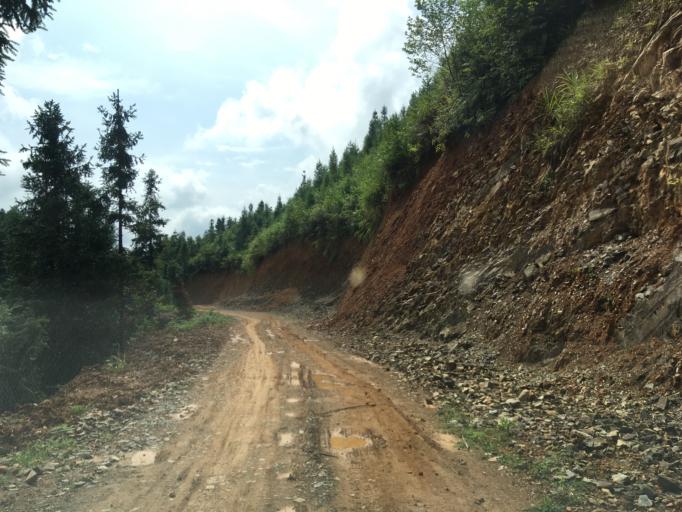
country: CN
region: Guangxi Zhuangzu Zizhiqu
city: Xinzhou
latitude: 24.8677
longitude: 105.8501
